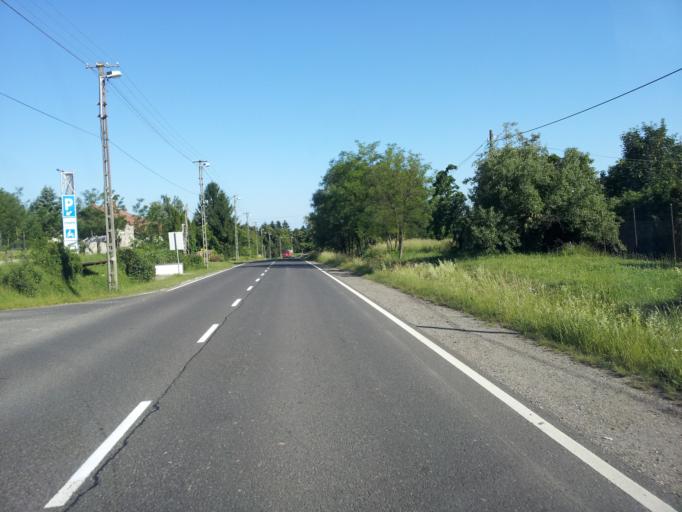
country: HU
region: Nograd
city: Nagyoroszi
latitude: 47.9949
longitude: 19.0999
